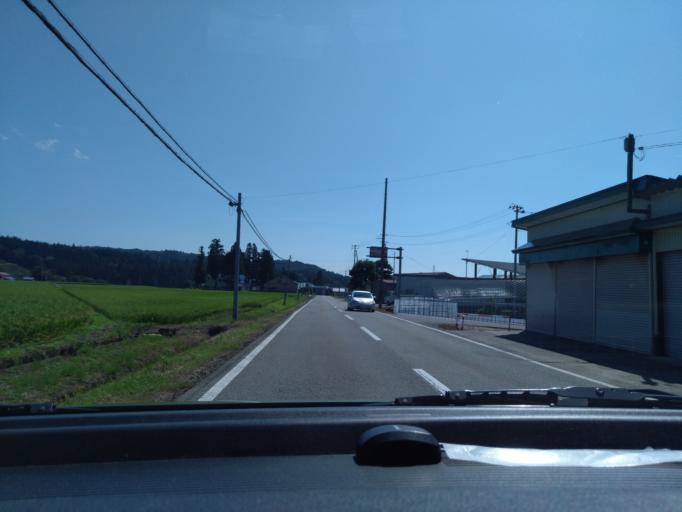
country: JP
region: Akita
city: Kakunodatemachi
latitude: 39.4782
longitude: 140.6121
